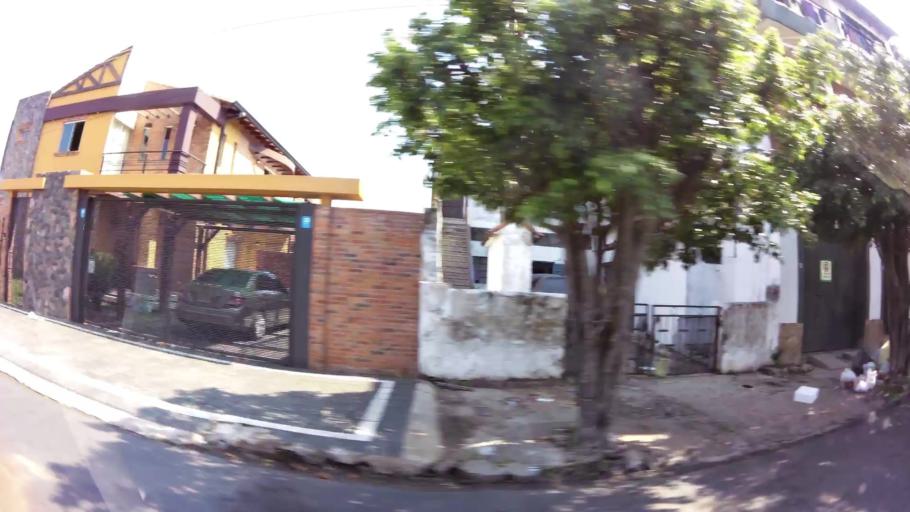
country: PY
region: Asuncion
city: Asuncion
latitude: -25.2901
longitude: -57.6561
